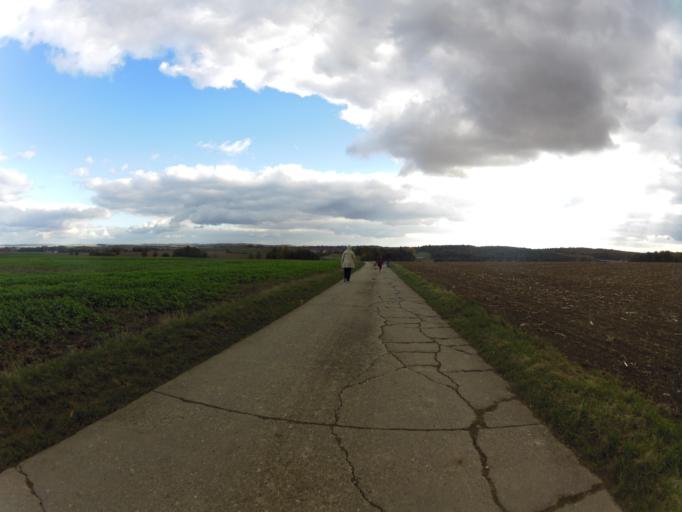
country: DE
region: Bavaria
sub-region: Regierungsbezirk Unterfranken
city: Kurnach
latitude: 49.8685
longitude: 10.0023
